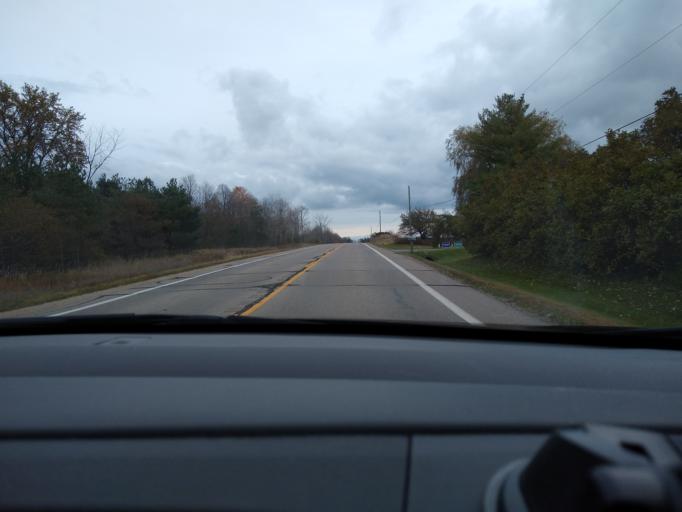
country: US
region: Michigan
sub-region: Delta County
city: Escanaba
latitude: 45.7439
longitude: -87.2733
